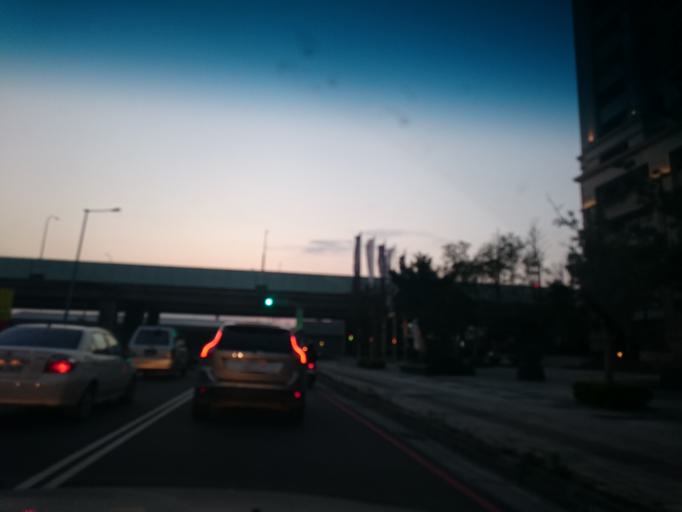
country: TW
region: Taiwan
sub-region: Taichung City
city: Taichung
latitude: 24.1763
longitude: 120.6351
